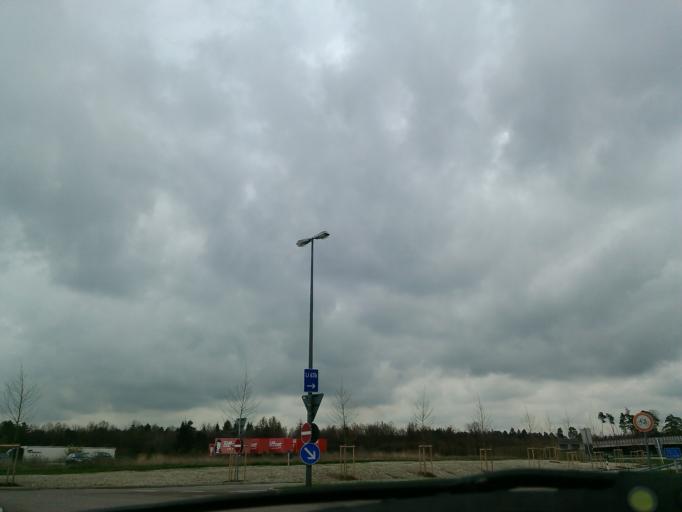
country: DE
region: Bavaria
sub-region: Upper Bavaria
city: Grafelfing
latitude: 48.1318
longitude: 11.4125
